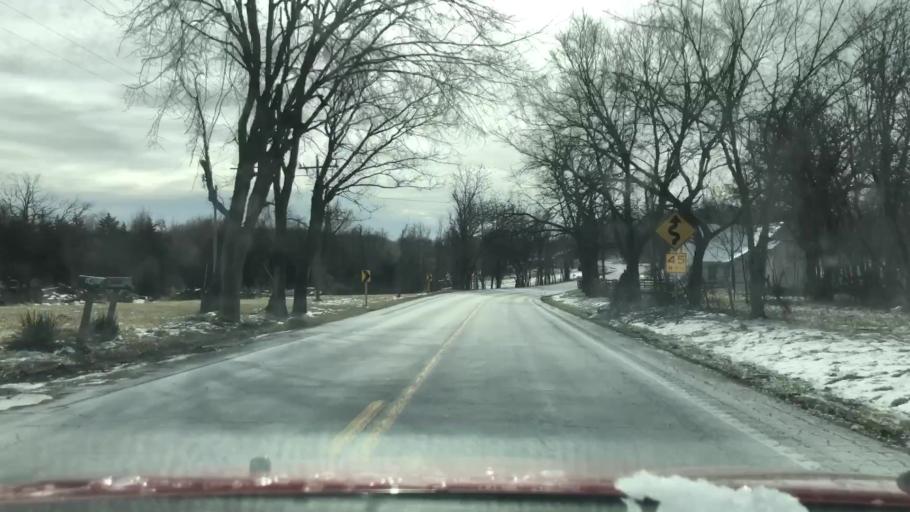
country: US
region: Missouri
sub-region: Jackson County
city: Oak Grove
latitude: 38.9421
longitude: -94.1321
